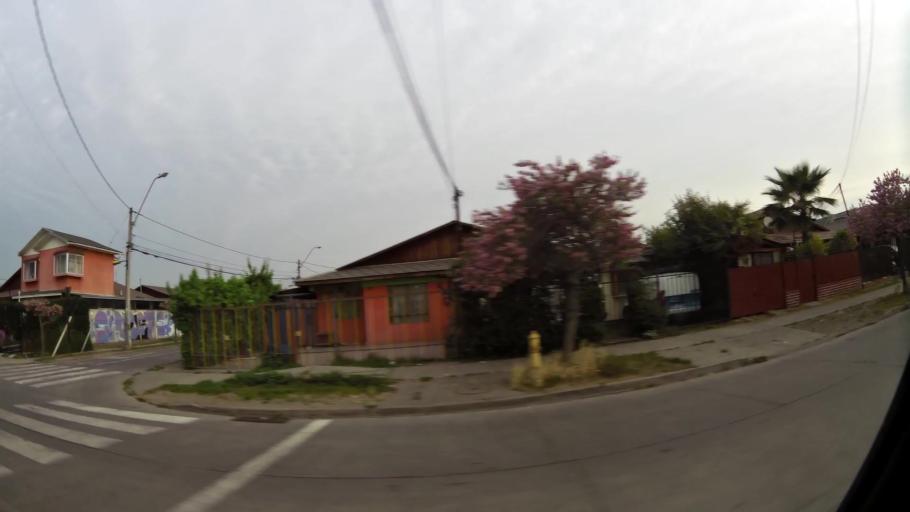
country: CL
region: Santiago Metropolitan
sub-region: Provincia de Santiago
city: Lo Prado
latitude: -33.5221
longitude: -70.7897
